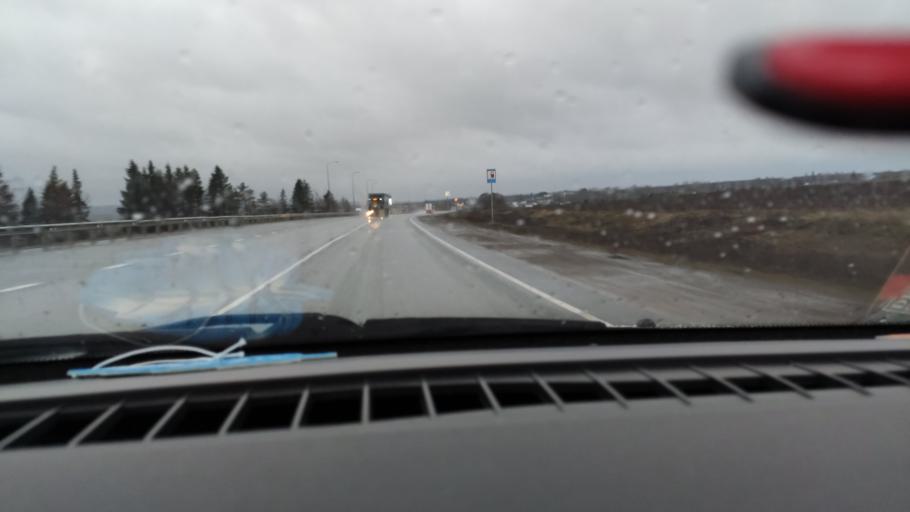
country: RU
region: Tatarstan
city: Mendeleyevsk
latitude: 56.0354
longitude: 52.3831
